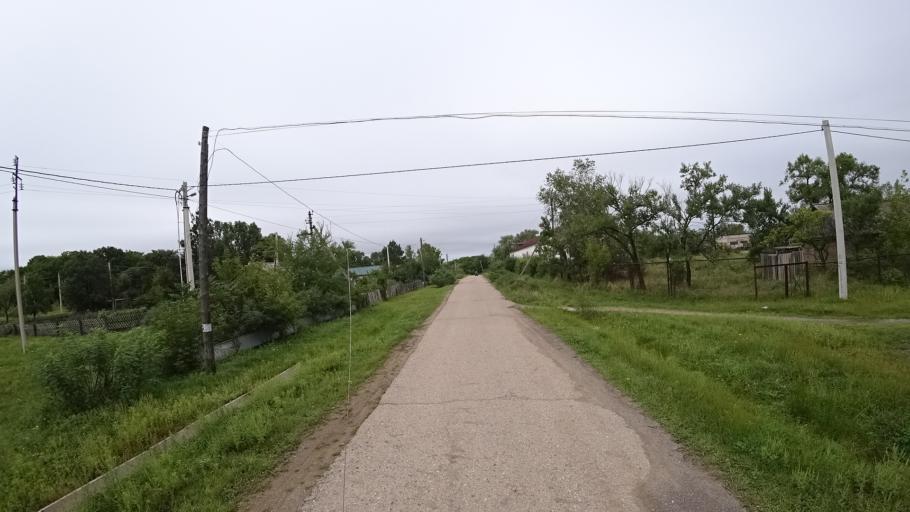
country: RU
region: Primorskiy
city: Monastyrishche
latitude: 44.0802
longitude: 132.5819
